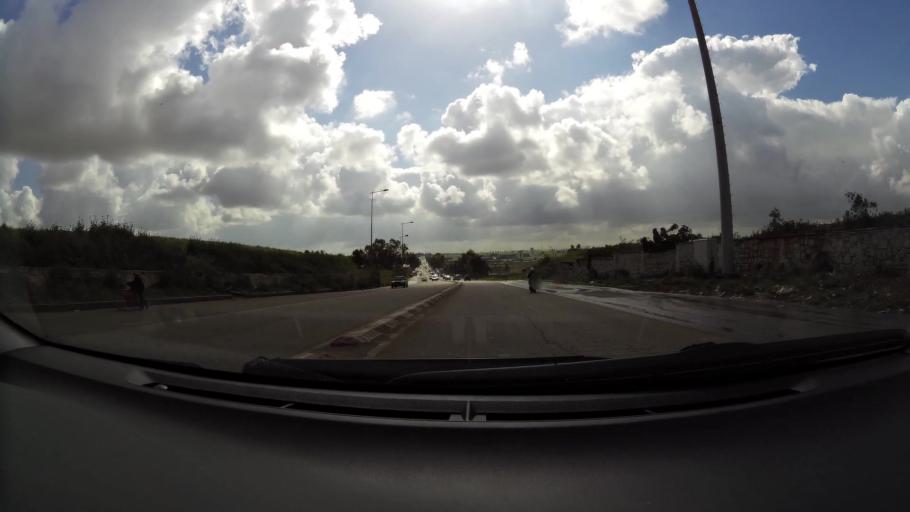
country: MA
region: Grand Casablanca
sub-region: Mediouna
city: Tit Mellil
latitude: 33.5682
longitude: -7.5141
